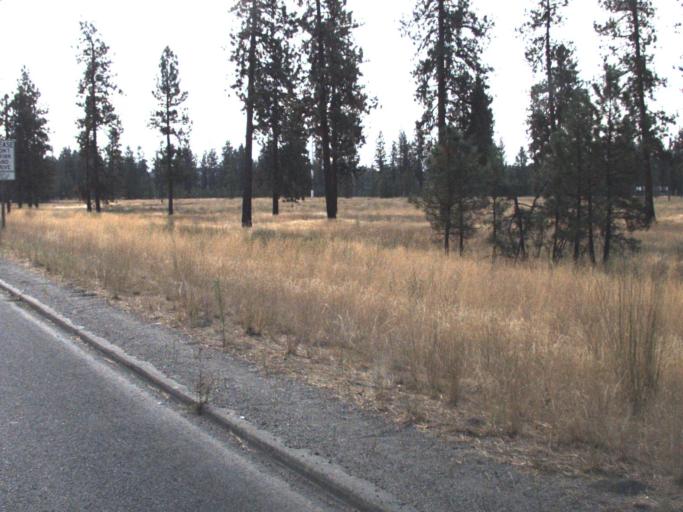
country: US
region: Washington
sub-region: Spokane County
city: Town and Country
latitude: 47.7330
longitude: -117.5052
